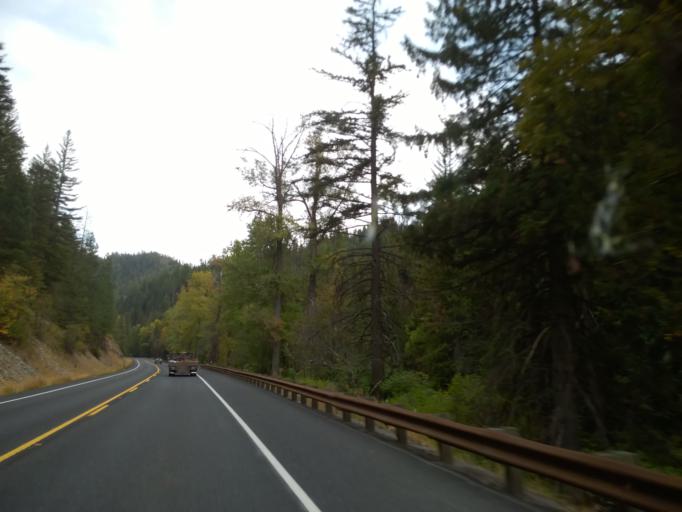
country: US
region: Washington
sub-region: Chelan County
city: Leavenworth
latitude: 47.4053
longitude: -120.6575
